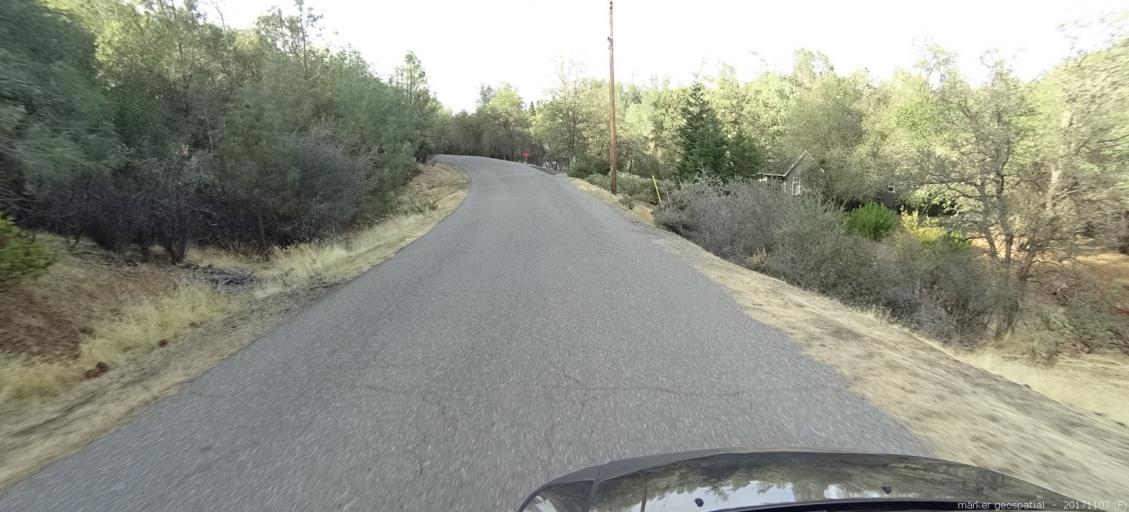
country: US
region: California
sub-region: Shasta County
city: Shasta
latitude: 40.5295
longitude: -122.4861
